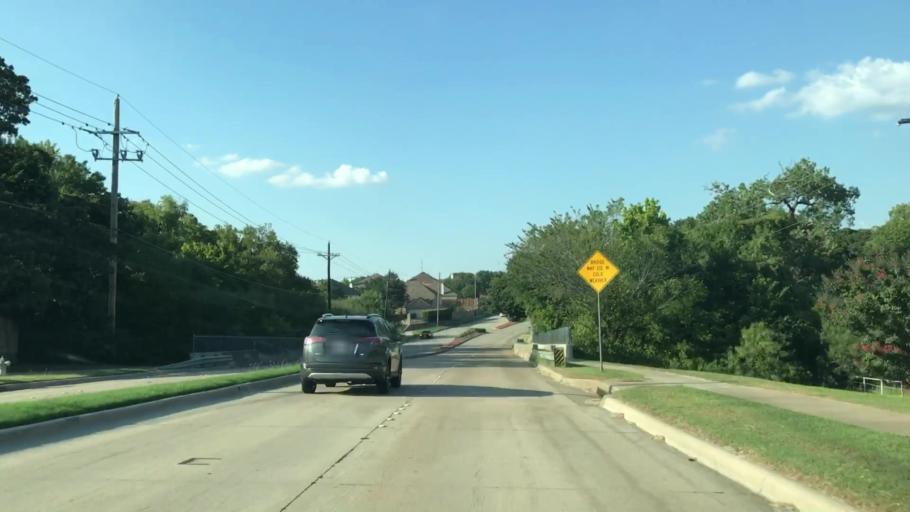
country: US
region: Texas
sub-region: Denton County
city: Lewisville
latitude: 33.0219
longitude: -97.0192
